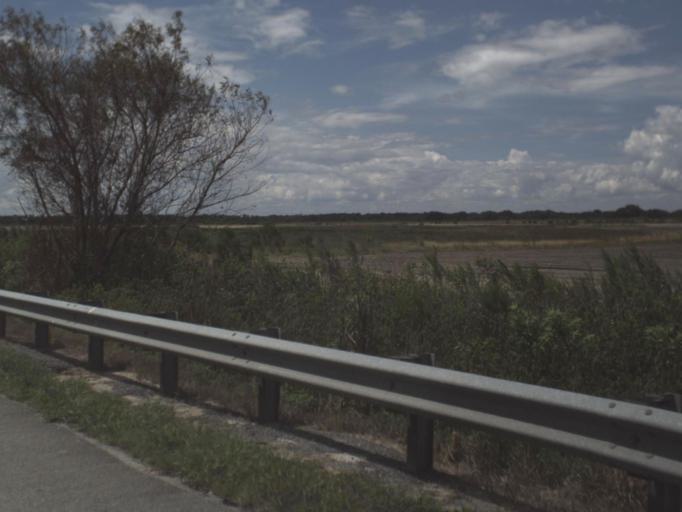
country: US
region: Florida
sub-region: Polk County
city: Babson Park
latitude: 27.8052
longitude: -81.2383
